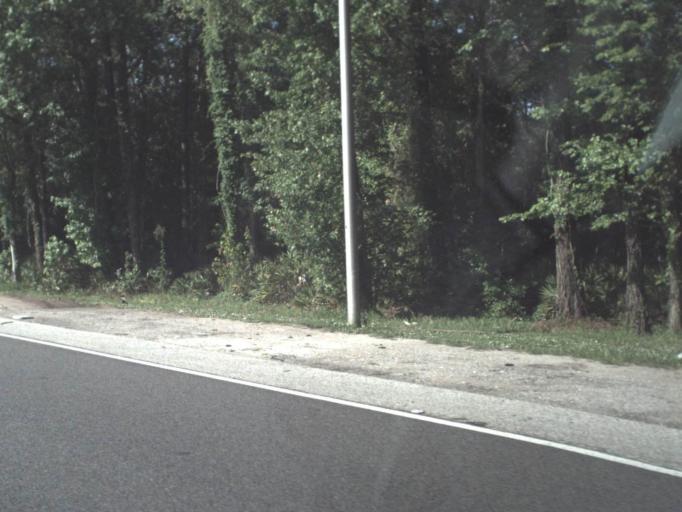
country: US
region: Florida
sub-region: Saint Johns County
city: Saint Augustine Shores
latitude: 29.7123
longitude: -81.3324
